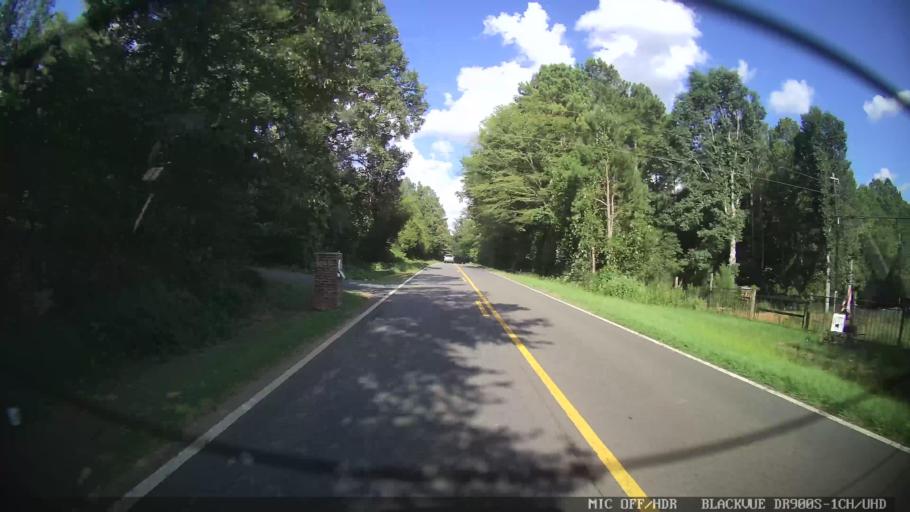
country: US
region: Georgia
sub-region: Bartow County
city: Euharlee
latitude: 34.1791
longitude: -85.0164
